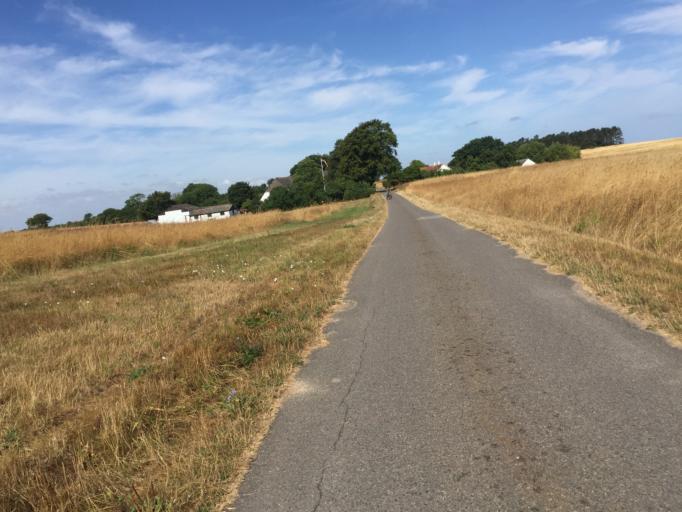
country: DK
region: Central Jutland
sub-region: Samso Kommune
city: Tranebjerg
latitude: 55.9548
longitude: 10.4222
